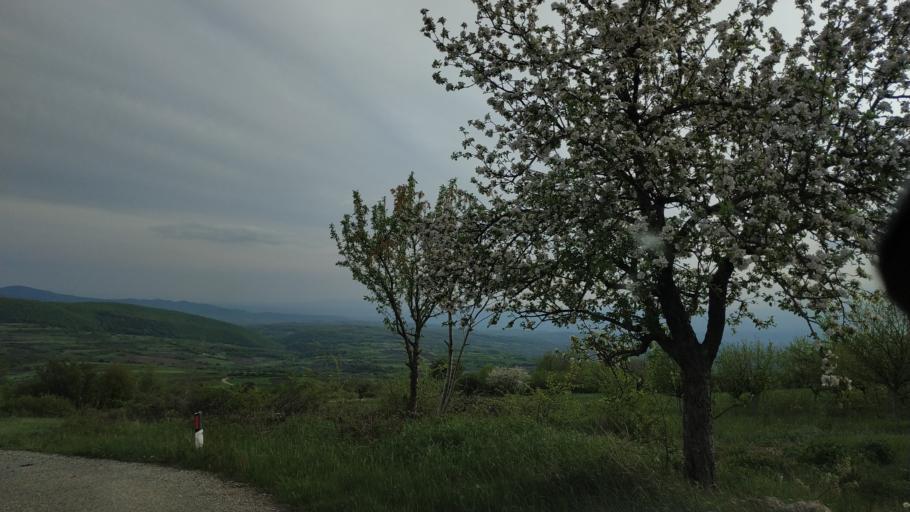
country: RS
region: Central Serbia
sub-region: Zajecarski Okrug
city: Soko Banja
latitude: 43.5349
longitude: 21.8784
